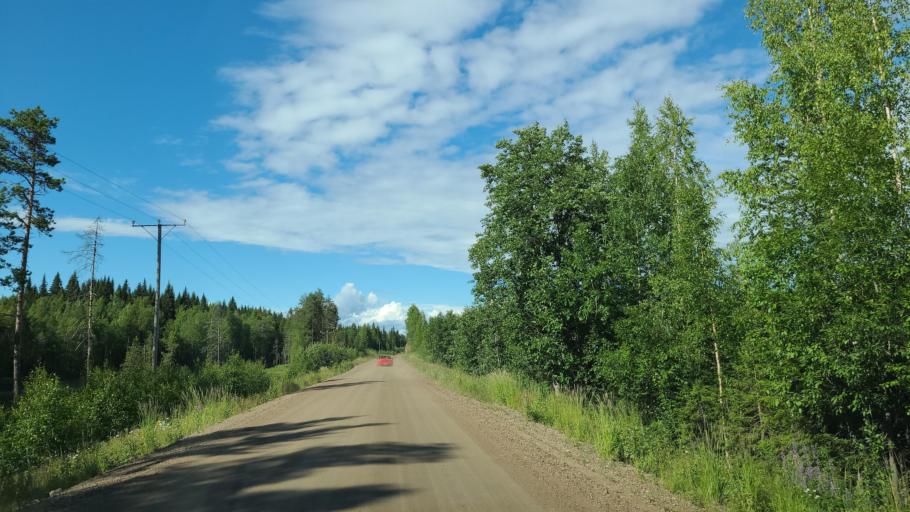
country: FI
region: Northern Savo
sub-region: Koillis-Savo
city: Kaavi
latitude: 62.9401
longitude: 28.7633
